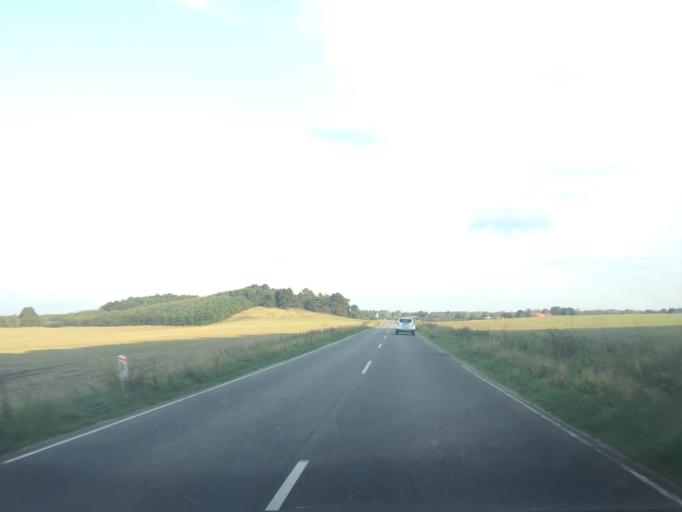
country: DK
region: Zealand
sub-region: Kalundborg Kommune
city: Hong
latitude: 55.5458
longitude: 11.3545
